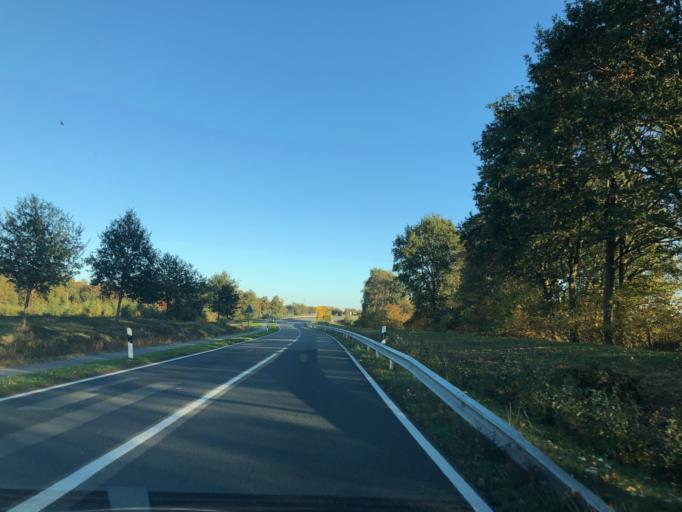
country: DE
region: Lower Saxony
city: Friesoythe
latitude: 53.0267
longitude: 7.7901
